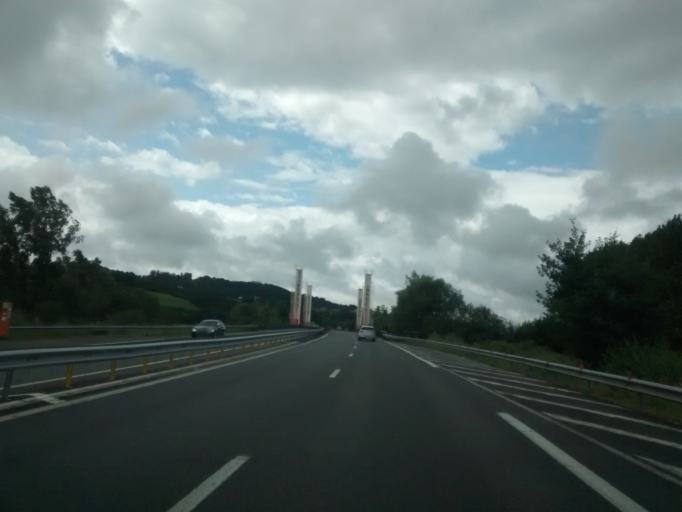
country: FR
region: Aquitaine
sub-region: Departement des Pyrenees-Atlantiques
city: Bardos
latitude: 43.5263
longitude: -1.2052
